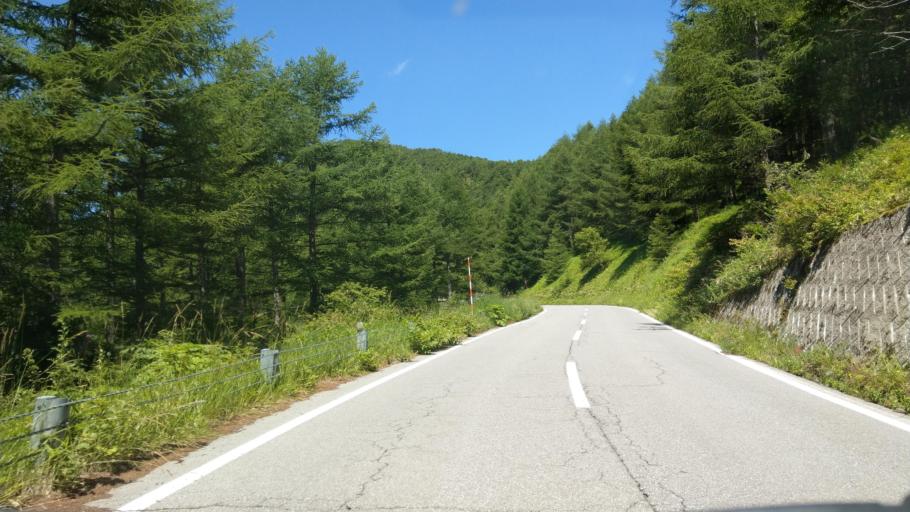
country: JP
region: Nagano
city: Komoro
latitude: 36.4008
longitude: 138.4718
